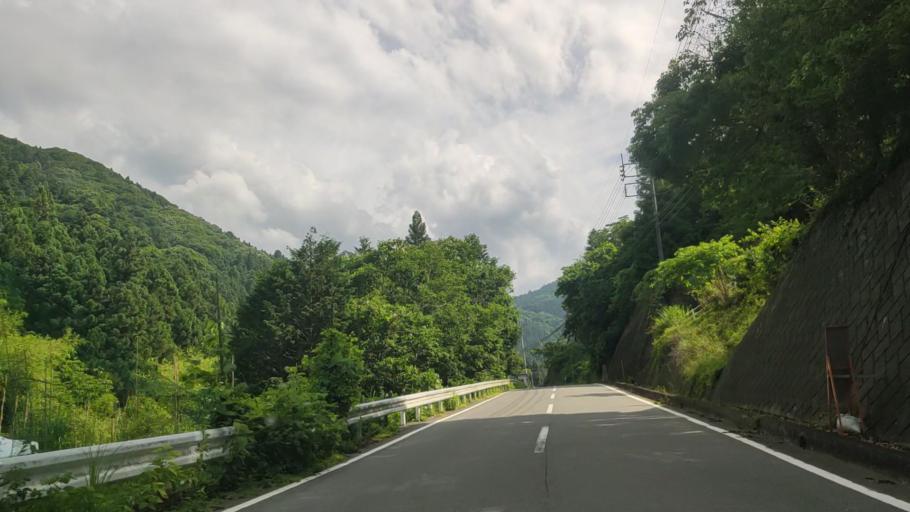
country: JP
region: Gunma
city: Tomioka
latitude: 36.1609
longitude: 138.7295
